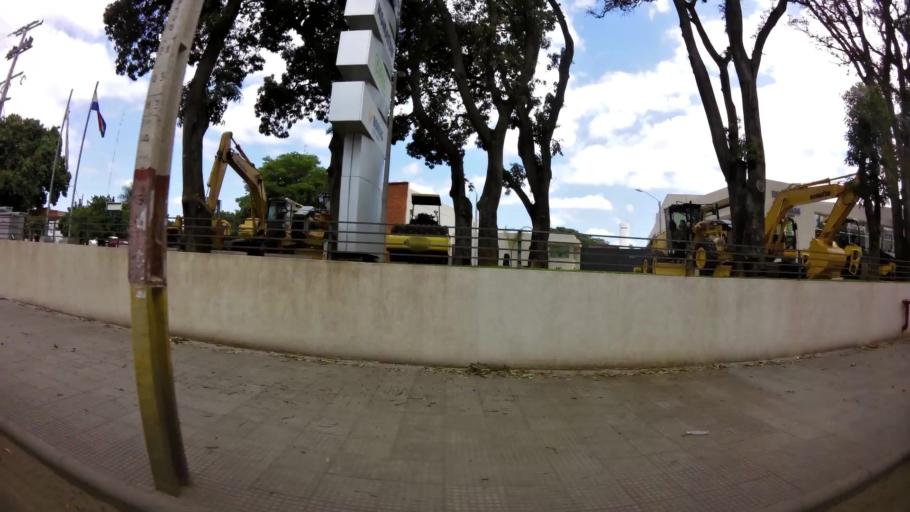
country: PY
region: Central
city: Fernando de la Mora
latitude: -25.3045
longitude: -57.5389
